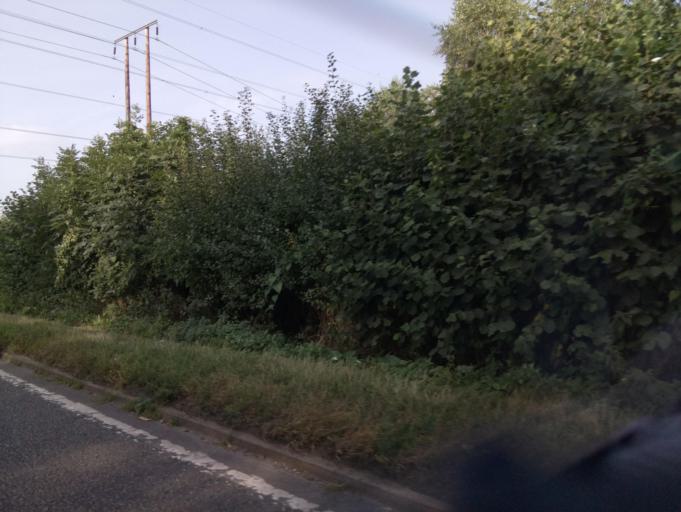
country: GB
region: England
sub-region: Warwickshire
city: Studley
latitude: 52.2547
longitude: -1.8883
